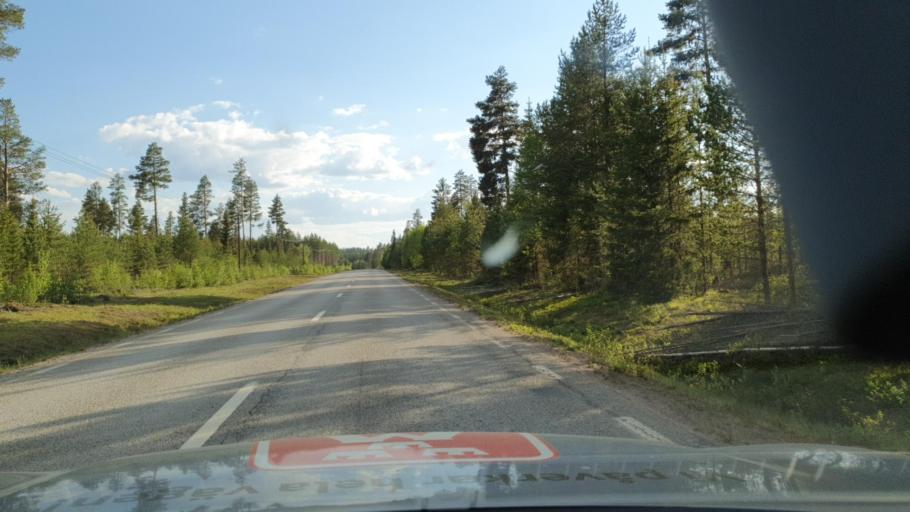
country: SE
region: Vaesterbotten
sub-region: Asele Kommun
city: Asele
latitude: 63.7838
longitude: 17.0397
